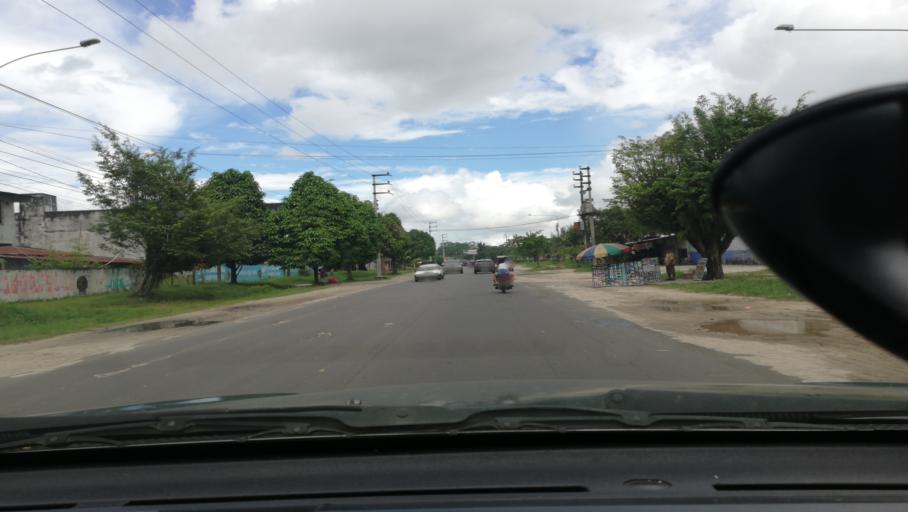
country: PE
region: Loreto
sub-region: Provincia de Maynas
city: Iquitos
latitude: -3.7859
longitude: -73.2998
